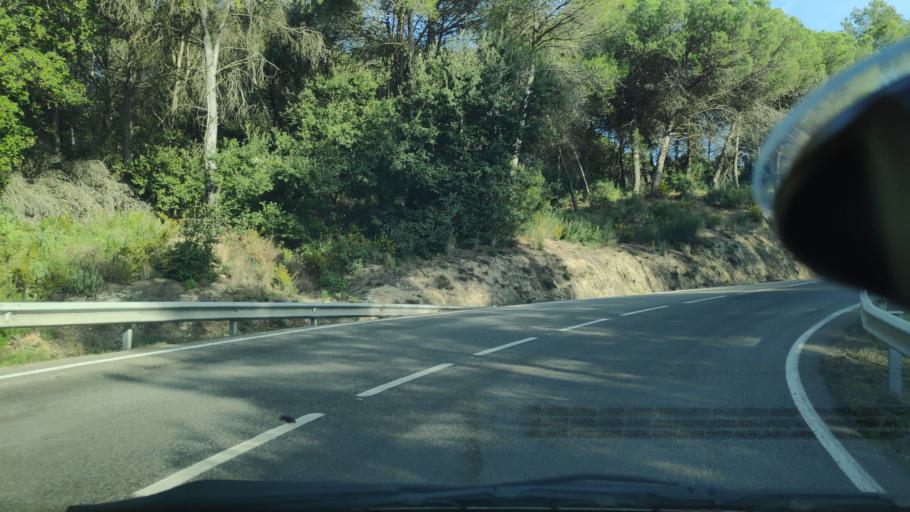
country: ES
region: Catalonia
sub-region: Provincia de Barcelona
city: Castellar del Valles
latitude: 41.6089
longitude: 2.0634
